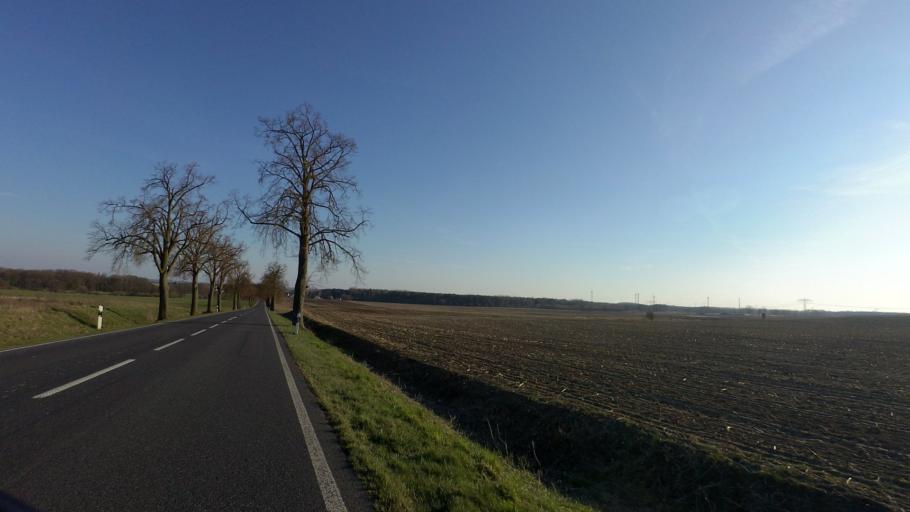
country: DE
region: Brandenburg
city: Britz
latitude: 52.8975
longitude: 13.8032
